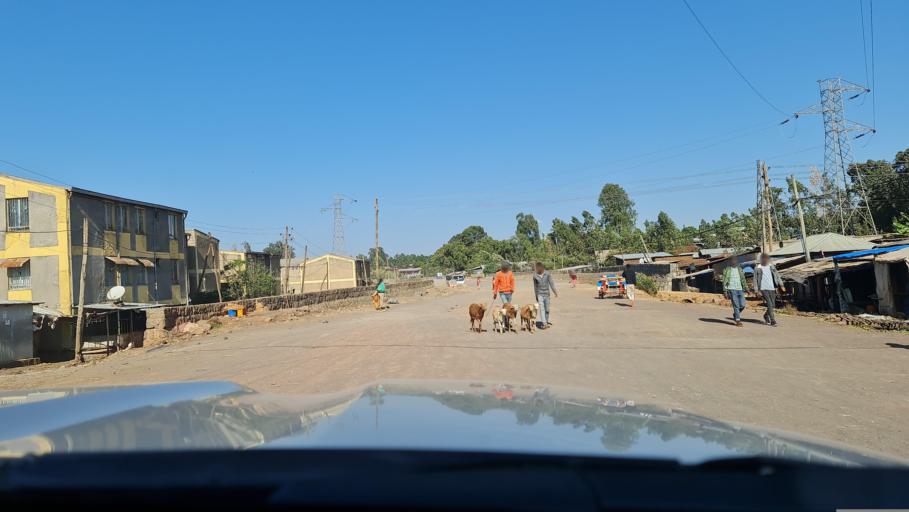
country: ET
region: Oromiya
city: Waliso
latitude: 8.5439
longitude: 37.9687
